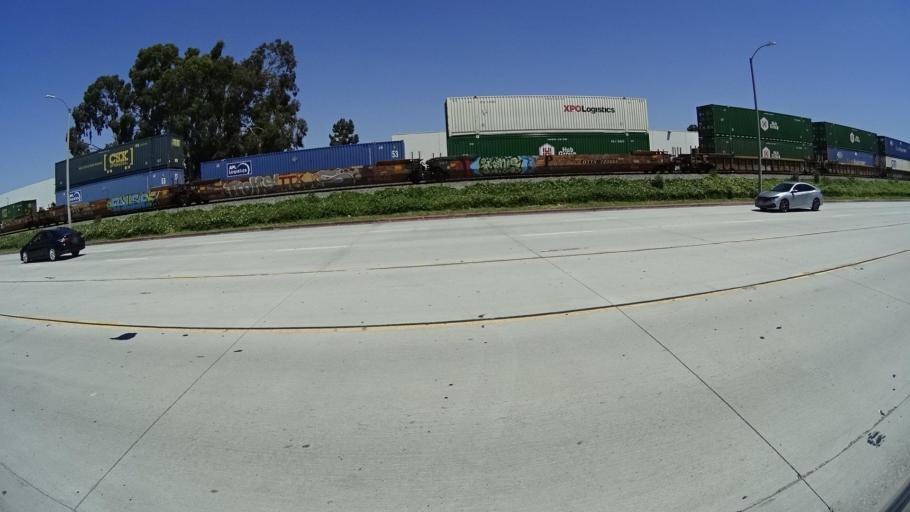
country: US
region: California
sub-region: Los Angeles County
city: La Puente
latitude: 34.0263
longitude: -117.9632
